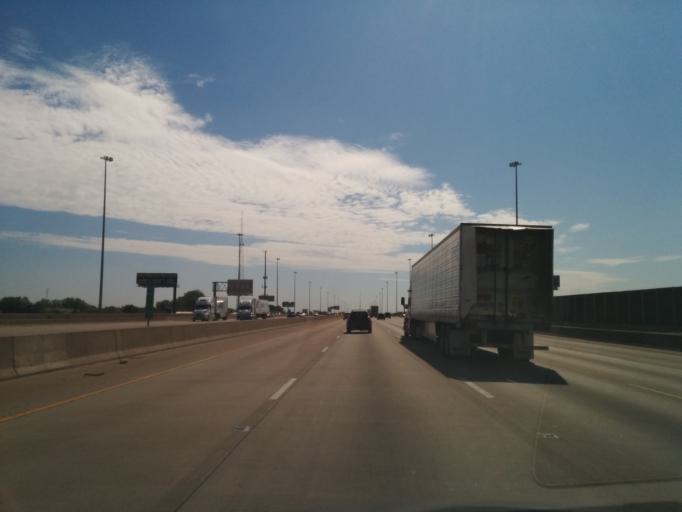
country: US
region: Illinois
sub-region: Cook County
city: Lansing
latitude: 41.5777
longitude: -87.5546
